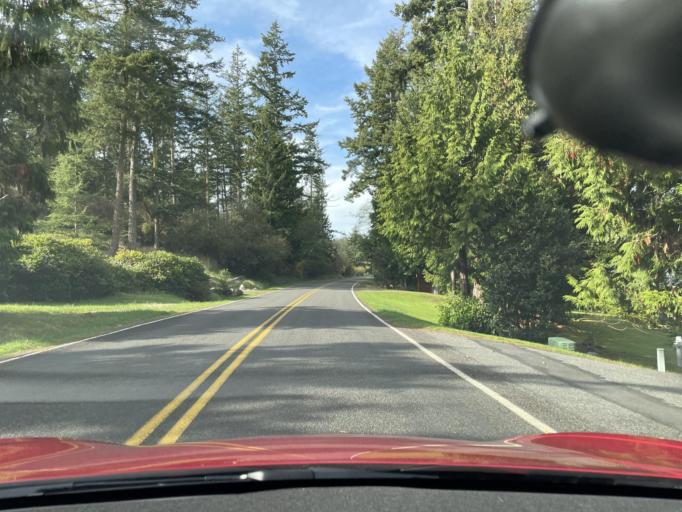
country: US
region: Washington
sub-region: San Juan County
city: Friday Harbor
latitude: 48.5260
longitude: -122.9768
